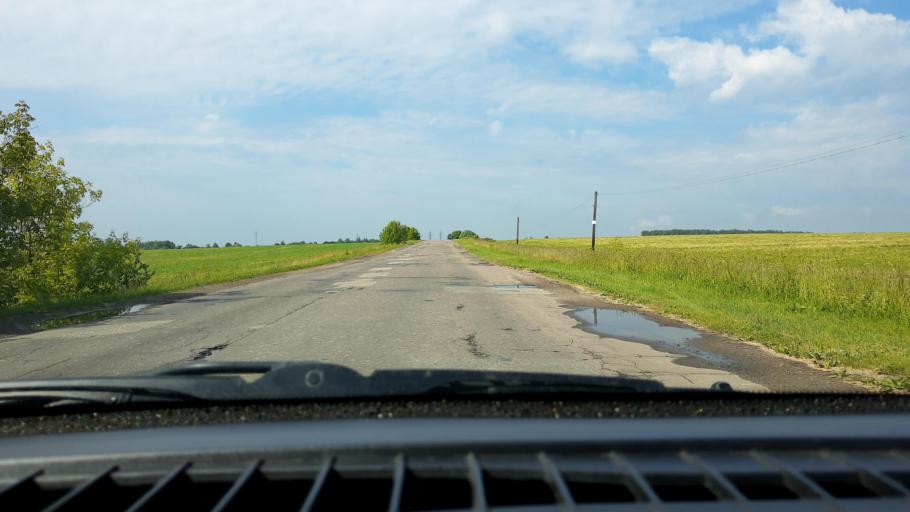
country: RU
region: Nizjnij Novgorod
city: Kstovo
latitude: 56.1143
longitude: 44.3043
